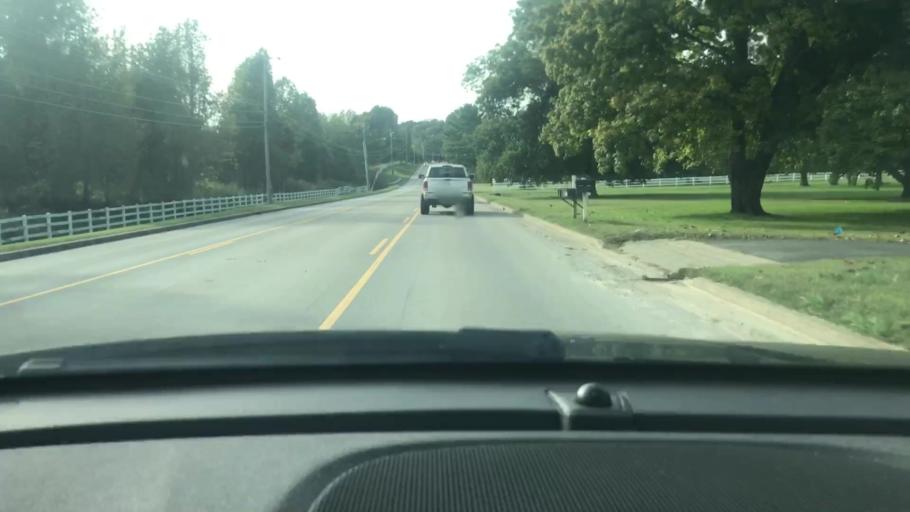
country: US
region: Tennessee
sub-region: Williamson County
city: Franklin
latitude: 35.9563
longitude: -86.8351
